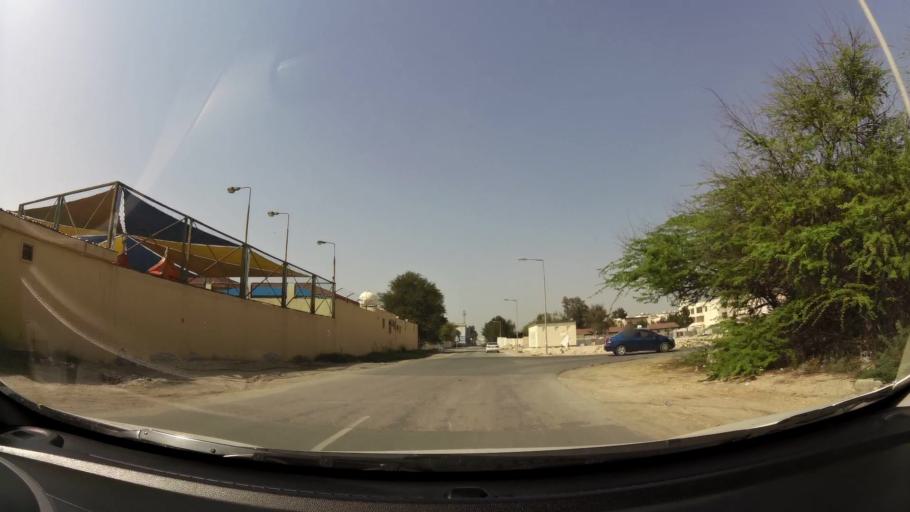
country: BH
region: Manama
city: Jidd Hafs
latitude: 26.2001
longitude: 50.4630
